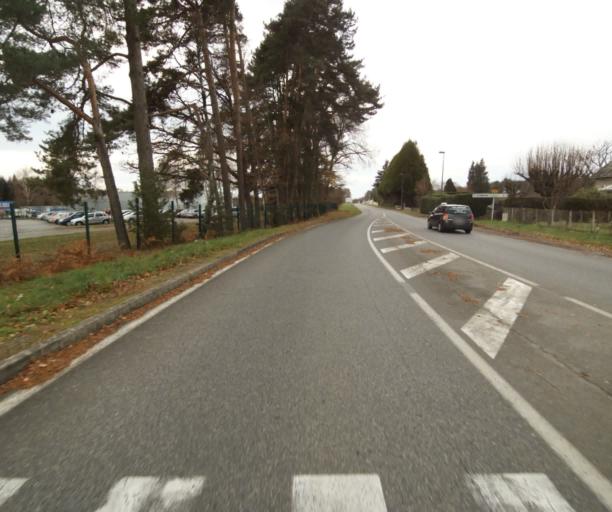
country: FR
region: Limousin
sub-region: Departement de la Correze
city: Saint-Mexant
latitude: 45.2710
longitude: 1.6650
